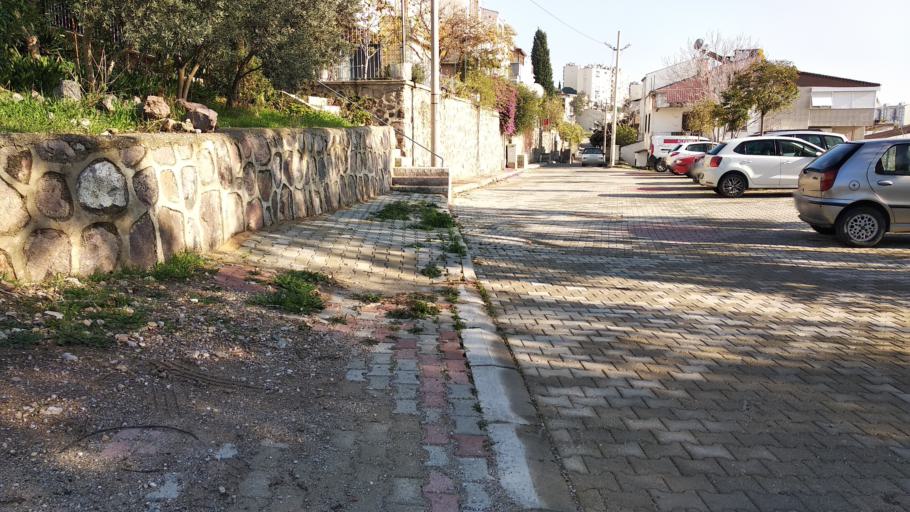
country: TR
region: Izmir
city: Karsiyaka
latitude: 38.4963
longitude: 27.0810
